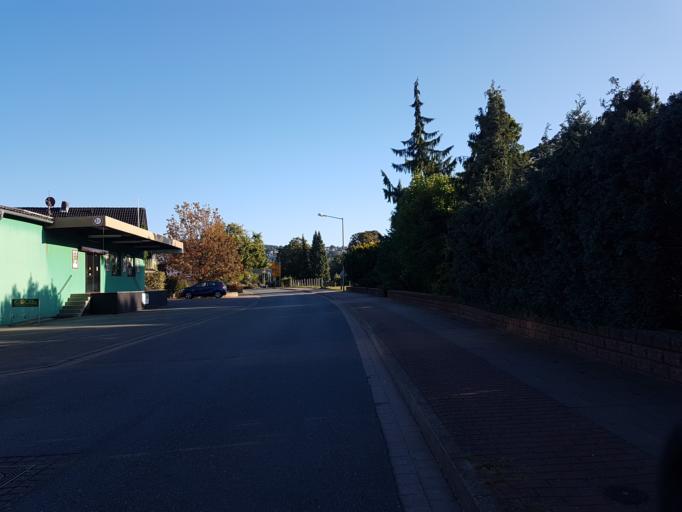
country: DE
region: North Rhine-Westphalia
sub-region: Regierungsbezirk Detmold
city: Vlotho
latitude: 52.1765
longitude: 8.8675
